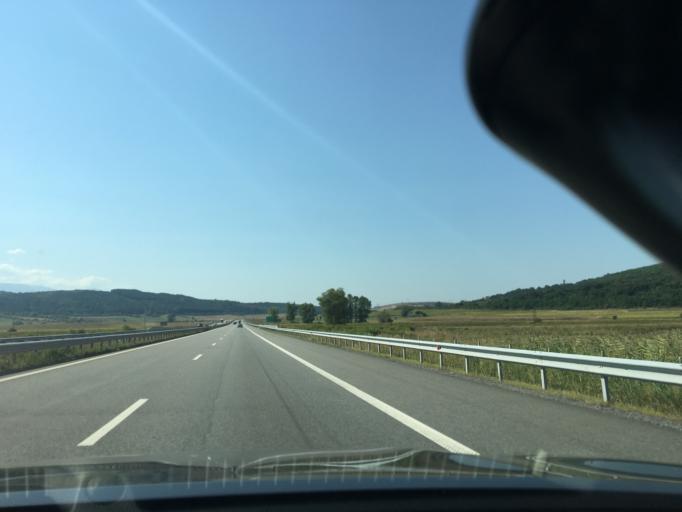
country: BG
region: Kyustendil
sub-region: Obshtina Bobovdol
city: Bobovdol
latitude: 42.4125
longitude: 23.1202
